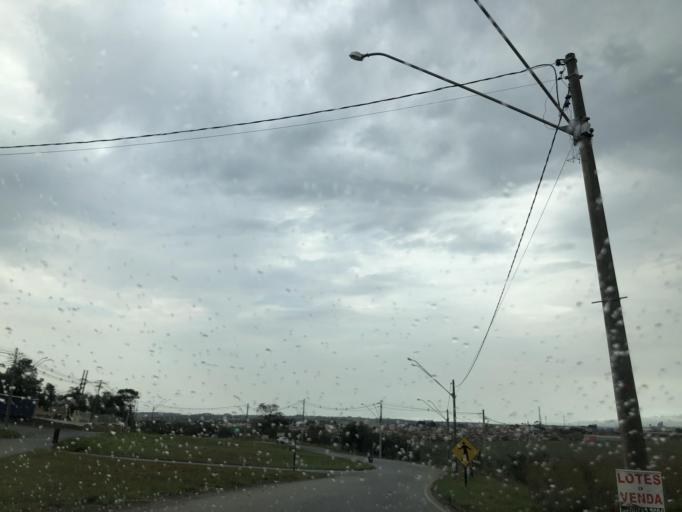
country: BR
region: Sao Paulo
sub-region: Salto De Pirapora
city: Salto de Pirapora
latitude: -23.6573
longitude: -47.5880
